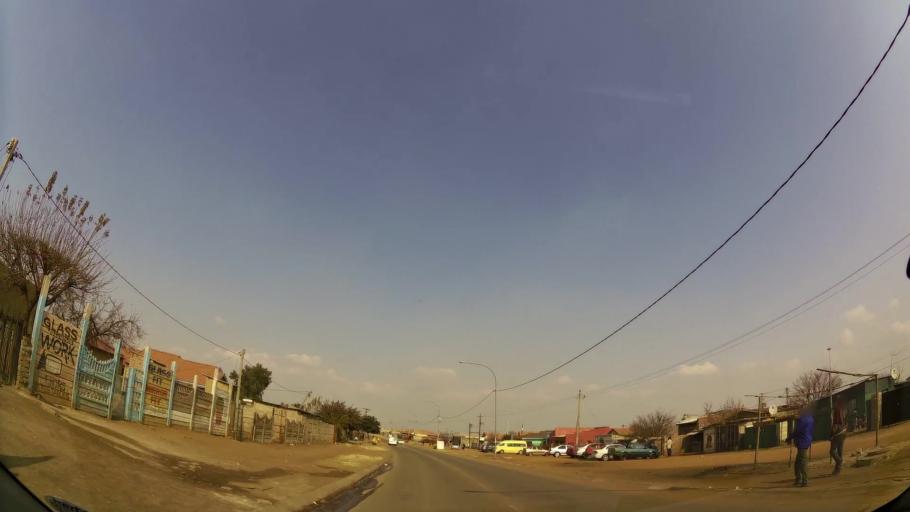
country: ZA
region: Gauteng
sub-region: Ekurhuleni Metropolitan Municipality
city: Springs
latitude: -26.1115
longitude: 28.4762
